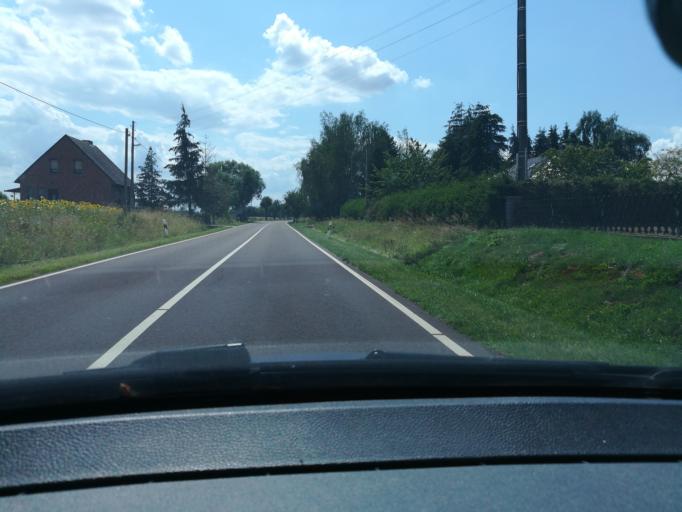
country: DE
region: Saxony-Anhalt
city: Rogatz
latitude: 52.3287
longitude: 11.7758
